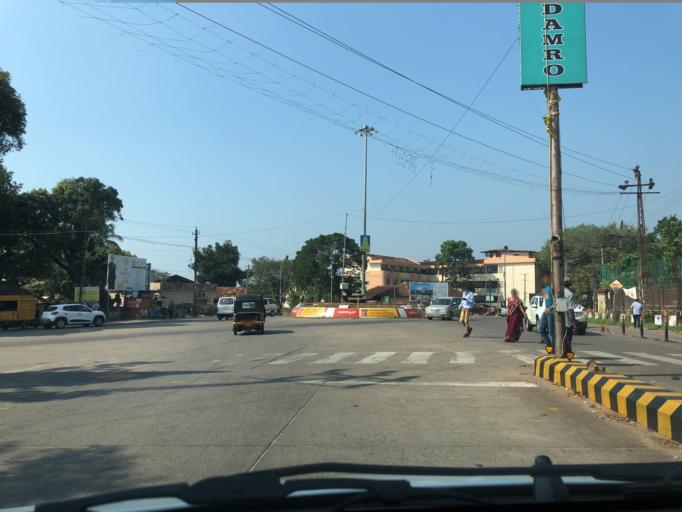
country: IN
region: Karnataka
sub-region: Dakshina Kannada
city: Mangalore
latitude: 12.8881
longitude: 74.8353
